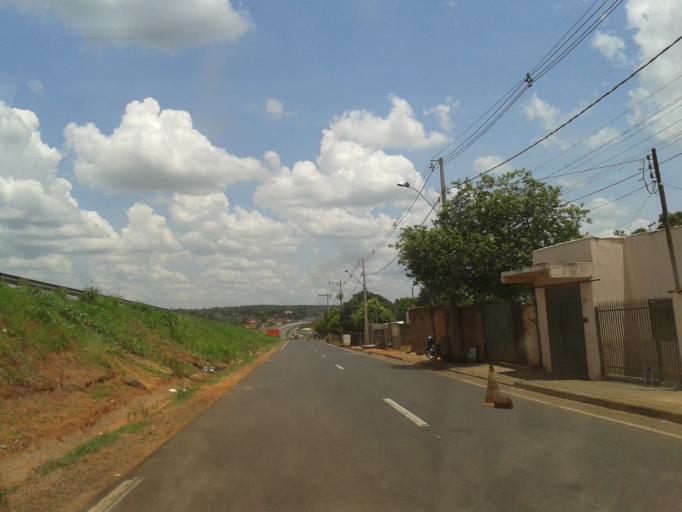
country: BR
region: Minas Gerais
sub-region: Monte Alegre De Minas
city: Monte Alegre de Minas
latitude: -18.8684
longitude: -48.8692
